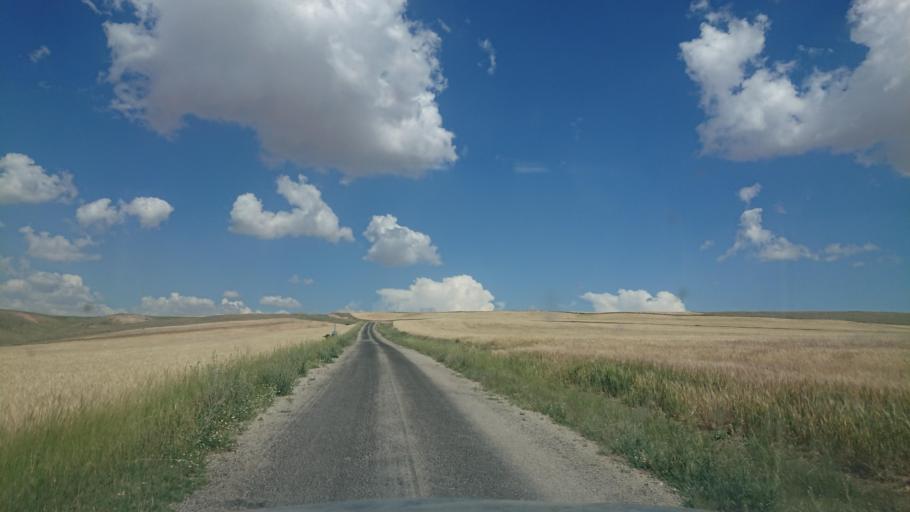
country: TR
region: Aksaray
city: Agacoren
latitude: 38.8063
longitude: 33.8029
